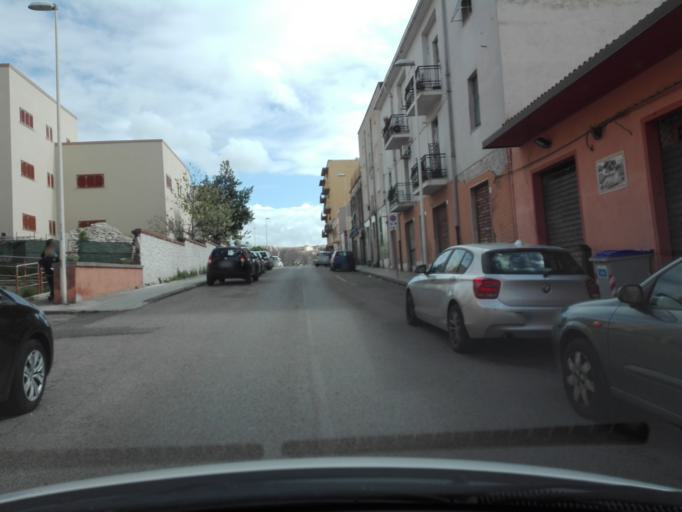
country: IT
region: Sardinia
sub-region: Provincia di Sassari
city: Sassari
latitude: 40.7348
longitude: 8.5662
